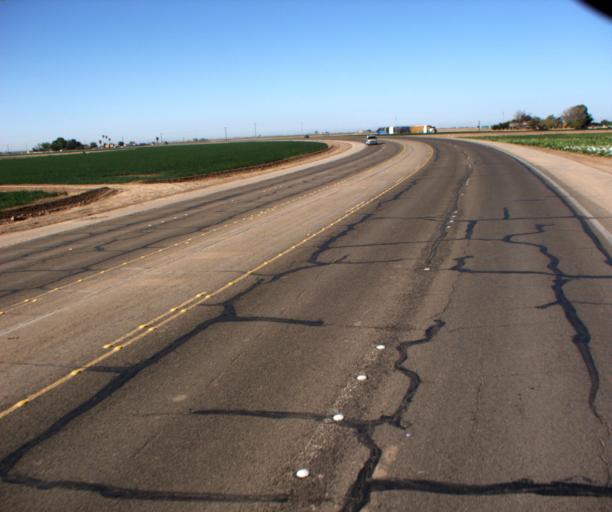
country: US
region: Arizona
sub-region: Yuma County
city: Somerton
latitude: 32.5962
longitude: -114.7652
